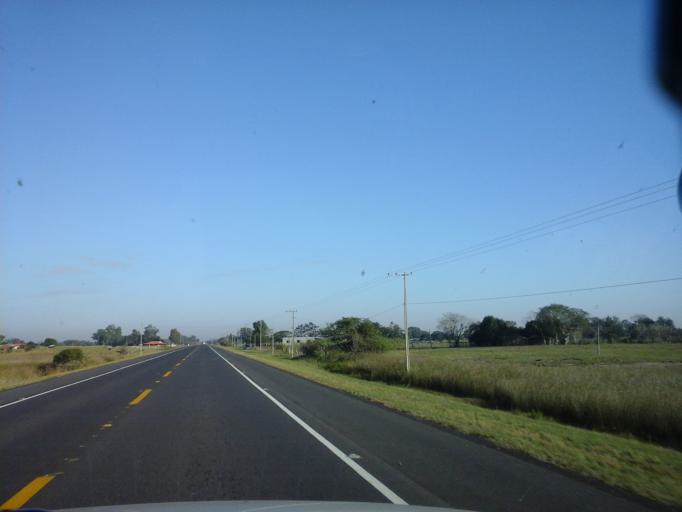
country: PY
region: Neembucu
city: Pilar
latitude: -26.8573
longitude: -58.0143
